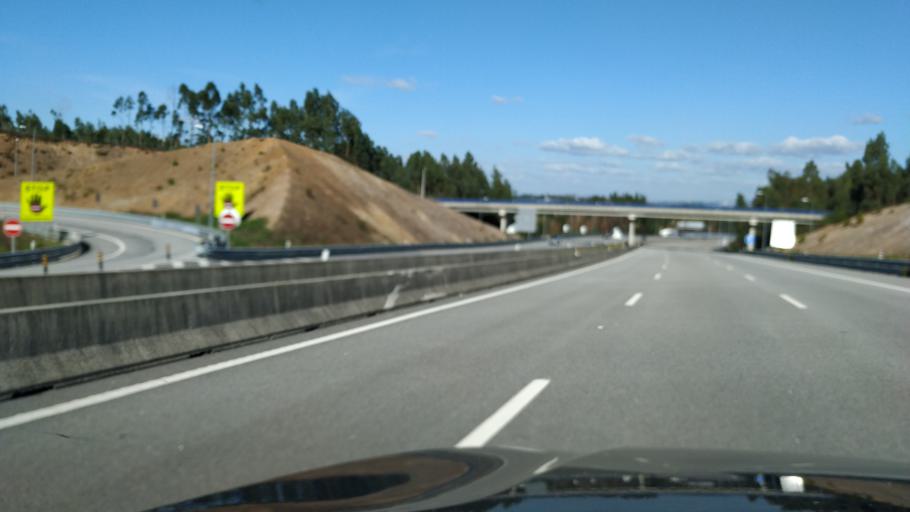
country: PT
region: Aveiro
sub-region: Santa Maria da Feira
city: Lobao
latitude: 41.0155
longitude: -8.4777
